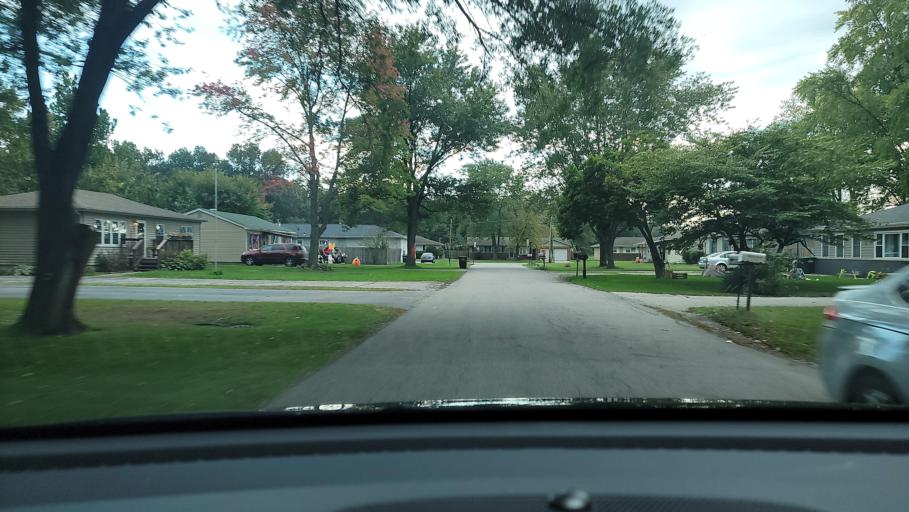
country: US
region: Indiana
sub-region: Porter County
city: Portage
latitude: 41.5695
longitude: -87.1799
